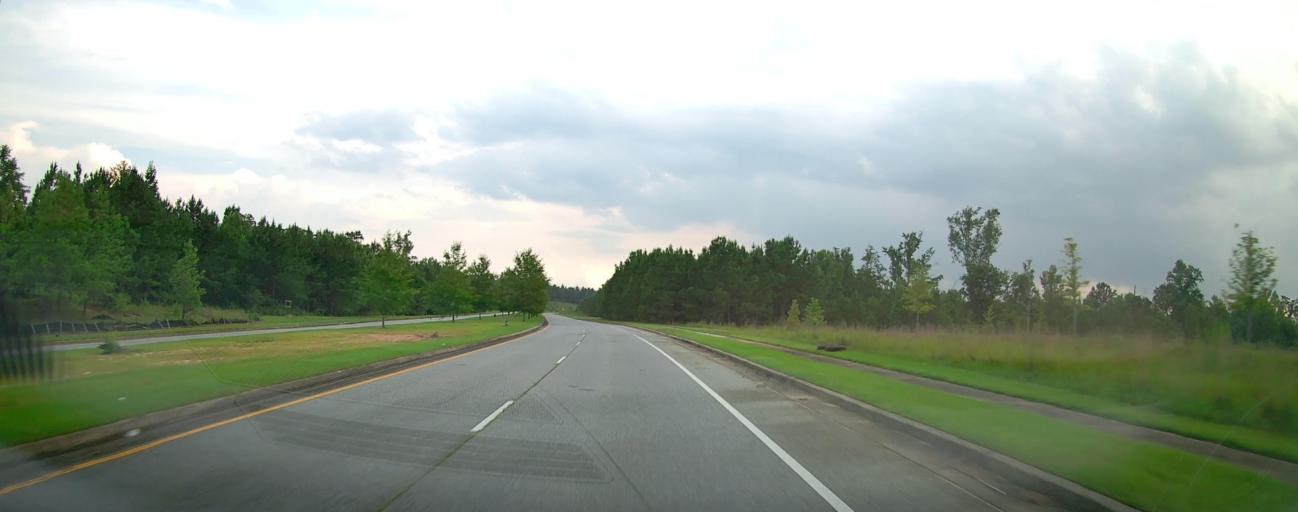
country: US
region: Georgia
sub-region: Muscogee County
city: Columbus
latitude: 32.5192
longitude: -84.8441
